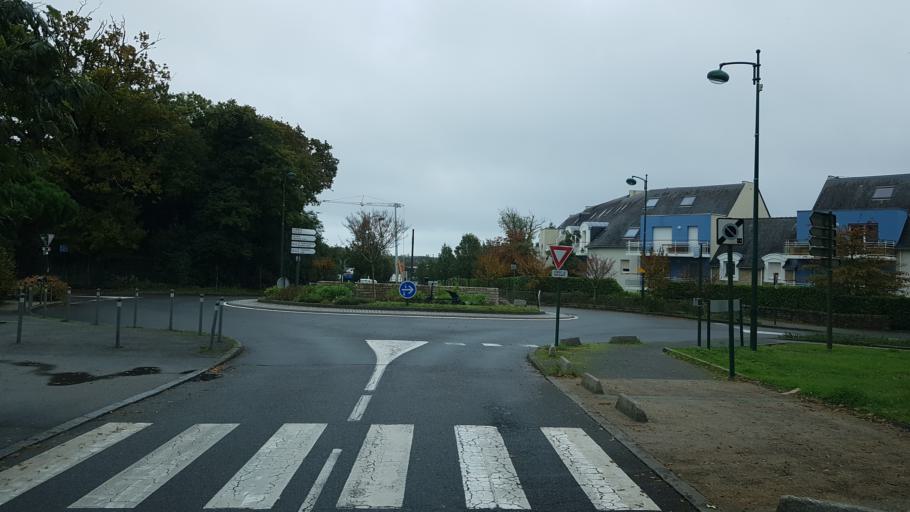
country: FR
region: Brittany
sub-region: Departement du Morbihan
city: Sarzeau
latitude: 47.5244
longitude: -2.7693
